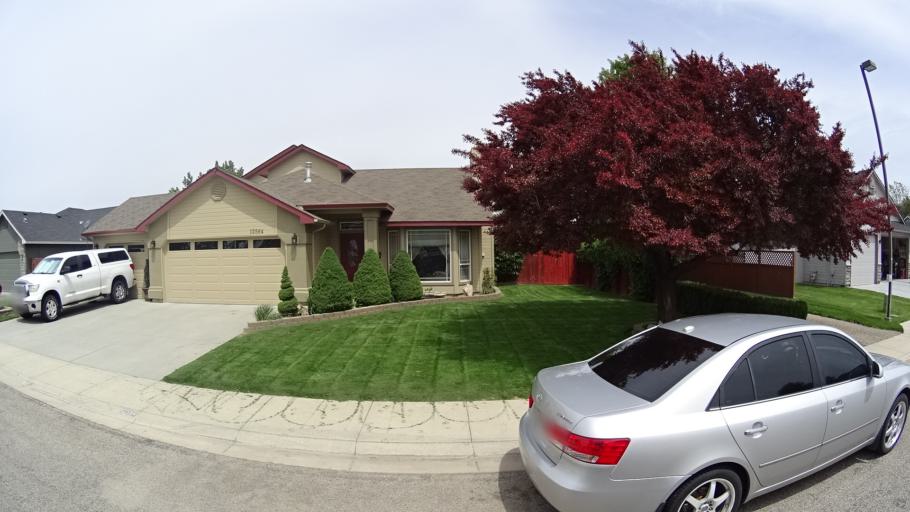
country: US
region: Idaho
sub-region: Ada County
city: Meridian
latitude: 43.5566
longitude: -116.3389
